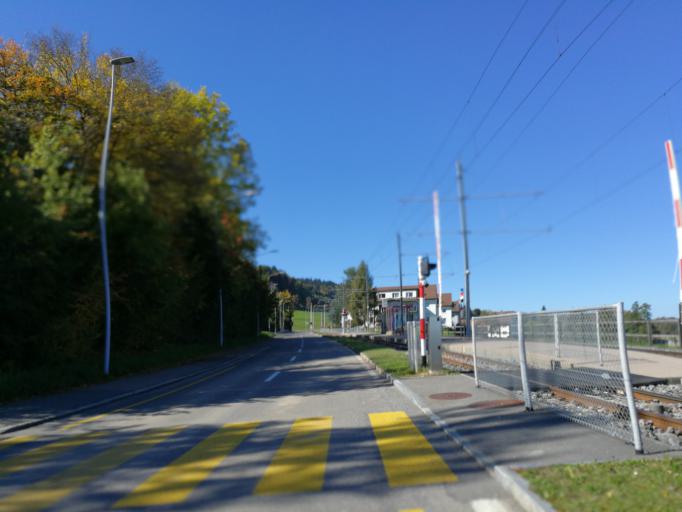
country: CH
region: Zurich
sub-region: Bezirk Uster
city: Hinteregg
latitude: 47.3125
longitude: 8.6747
